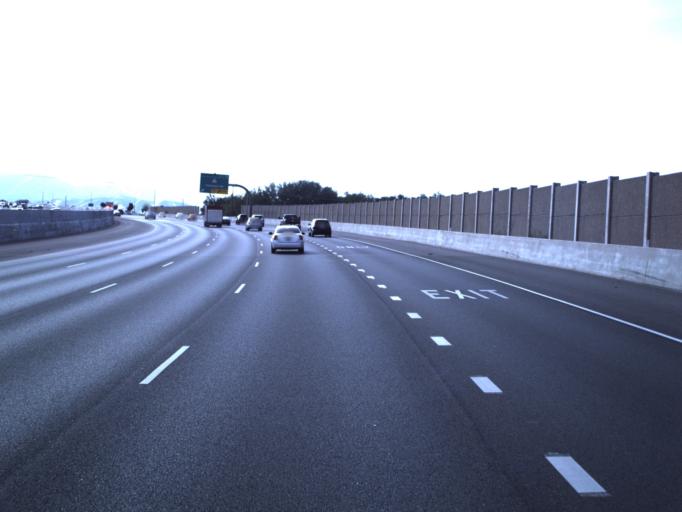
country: US
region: Utah
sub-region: Salt Lake County
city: Taylorsville
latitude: 40.6444
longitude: -111.9293
